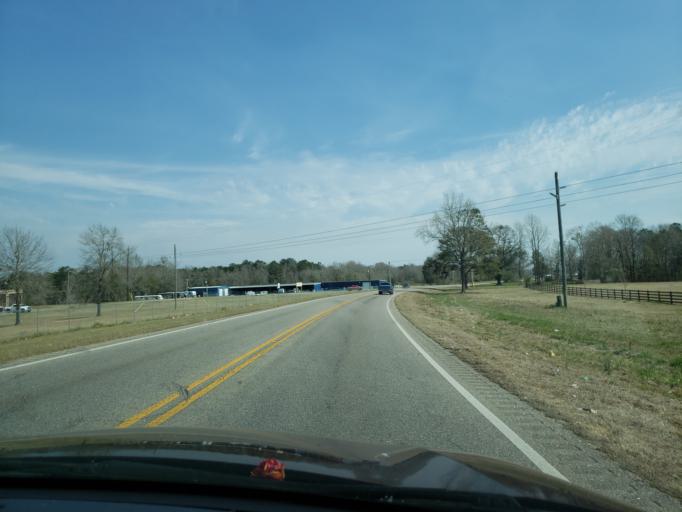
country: US
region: Alabama
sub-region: Elmore County
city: Elmore
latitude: 32.5316
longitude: -86.3415
